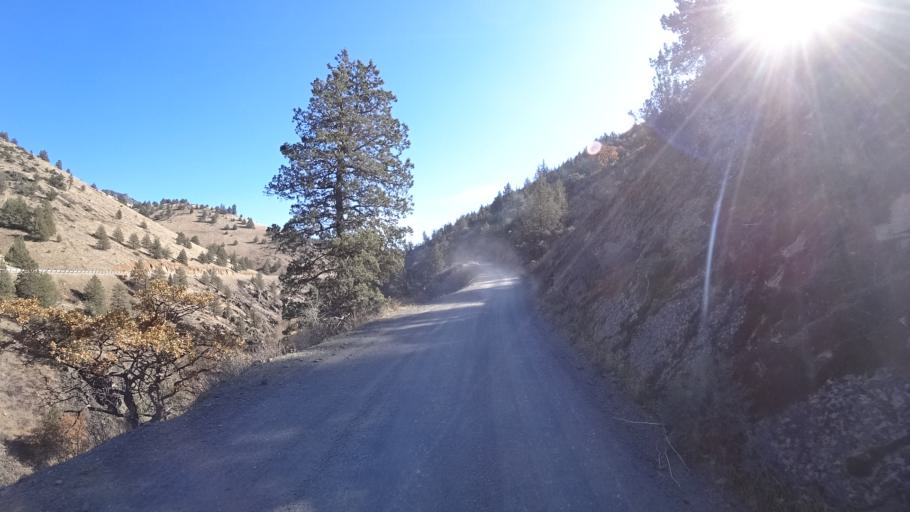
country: US
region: California
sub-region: Siskiyou County
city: Yreka
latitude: 41.7899
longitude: -122.6079
